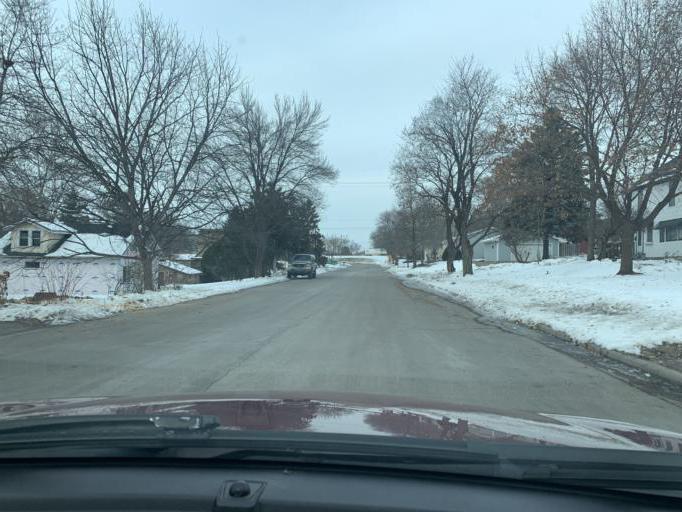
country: US
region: Minnesota
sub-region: Washington County
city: Saint Paul Park
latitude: 44.8468
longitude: -92.9929
